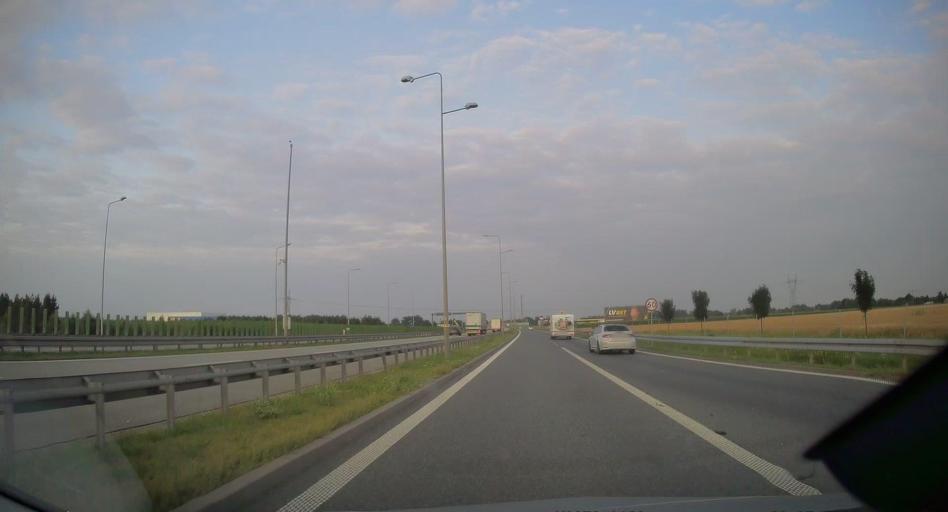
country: PL
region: Lodz Voivodeship
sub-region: Piotrkow Trybunalski
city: Piotrkow Trybunalski
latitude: 51.4422
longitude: 19.6727
